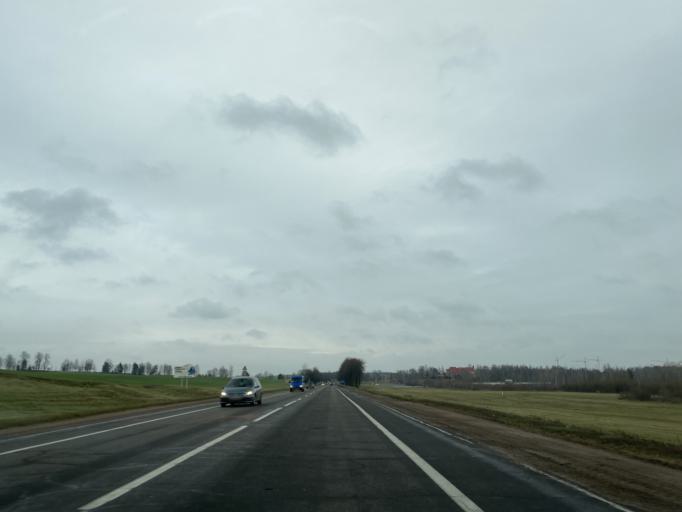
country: BY
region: Minsk
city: Horad Smalyavichy
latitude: 54.0431
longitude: 28.0570
